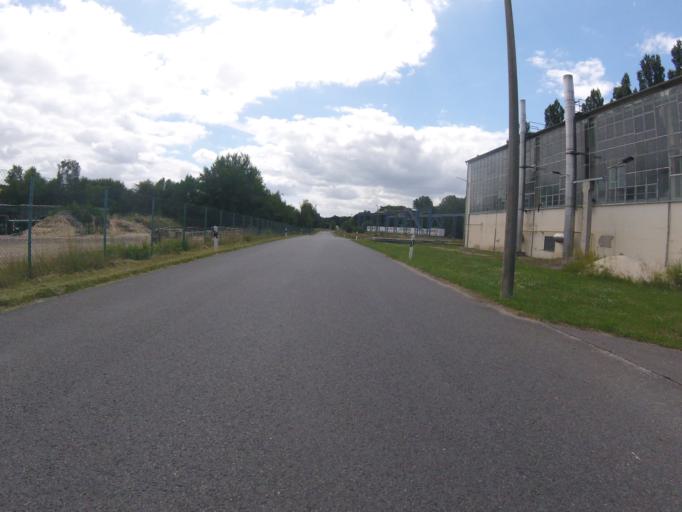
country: DE
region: Brandenburg
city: Mittenwalde
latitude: 52.2482
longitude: 13.5186
